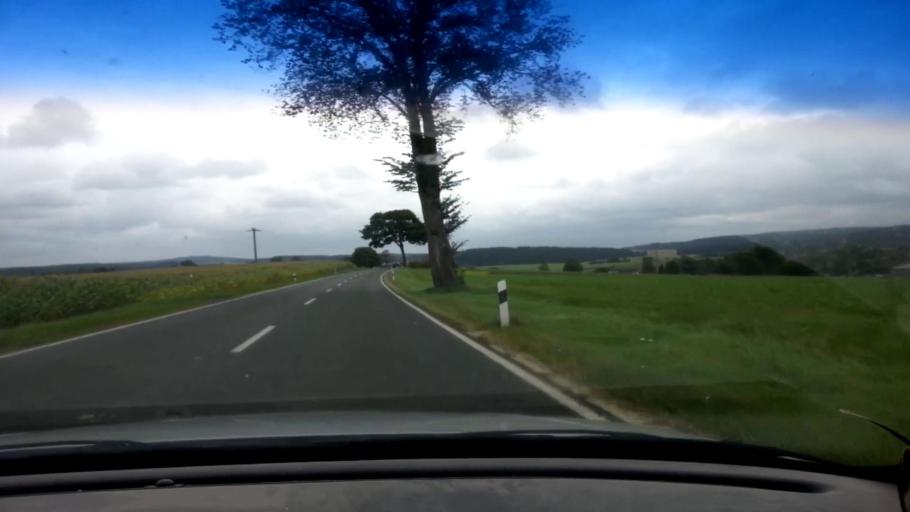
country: DE
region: Bavaria
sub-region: Upper Franconia
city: Roslau
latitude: 50.0814
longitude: 11.9542
